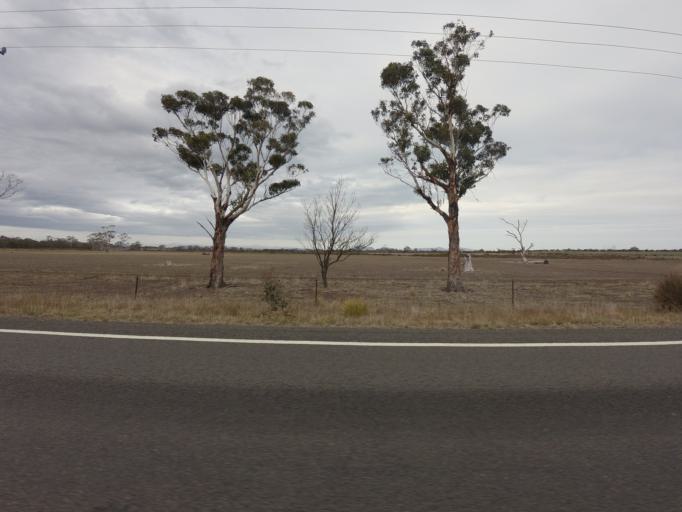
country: AU
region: Tasmania
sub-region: Break O'Day
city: St Helens
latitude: -42.0895
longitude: 148.0667
